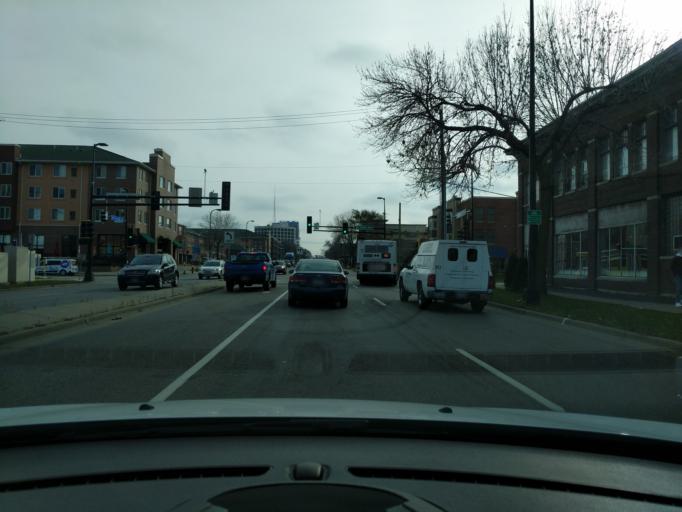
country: US
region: Minnesota
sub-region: Ramsey County
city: Lauderdale
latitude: 44.9736
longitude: -93.2220
